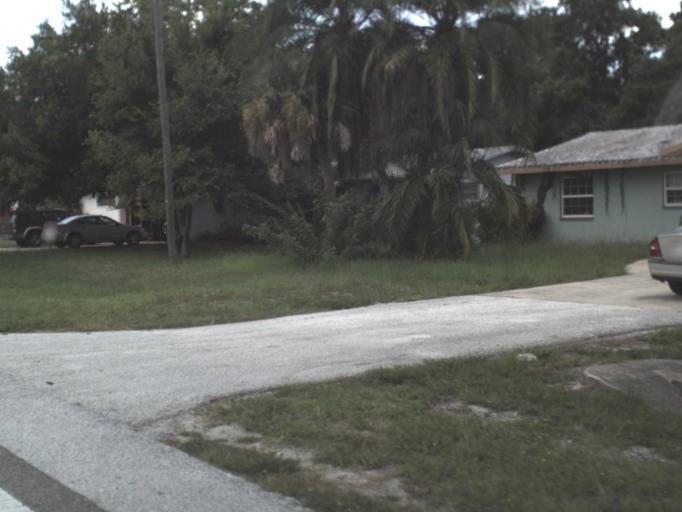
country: US
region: Florida
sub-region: Pinellas County
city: Dunedin
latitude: 27.9733
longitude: -82.7445
